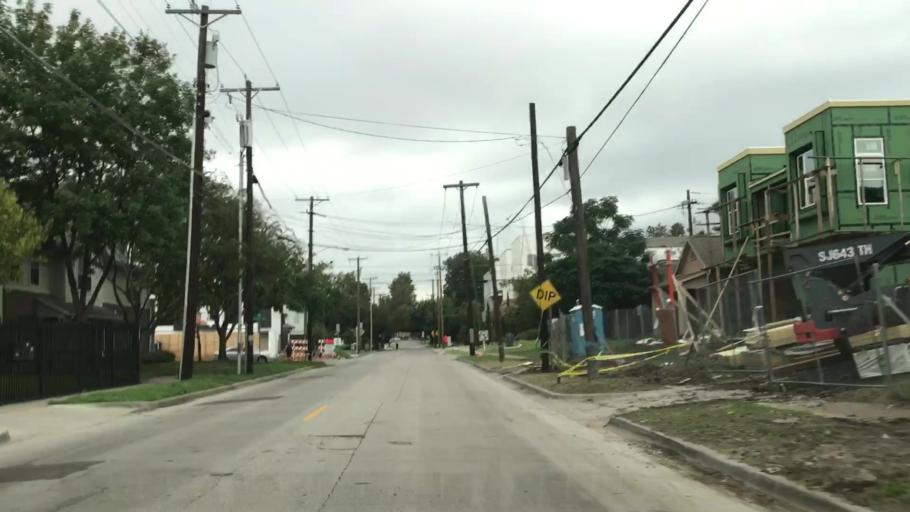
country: US
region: Texas
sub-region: Dallas County
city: Highland Park
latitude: 32.8063
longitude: -96.7844
